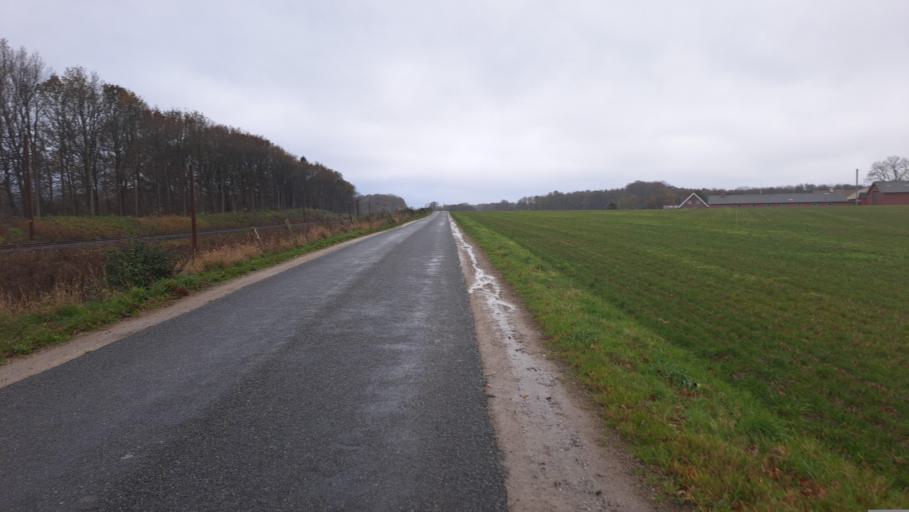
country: DK
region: Central Jutland
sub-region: Hedensted Kommune
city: Hedensted
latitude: 55.8265
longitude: 9.7304
